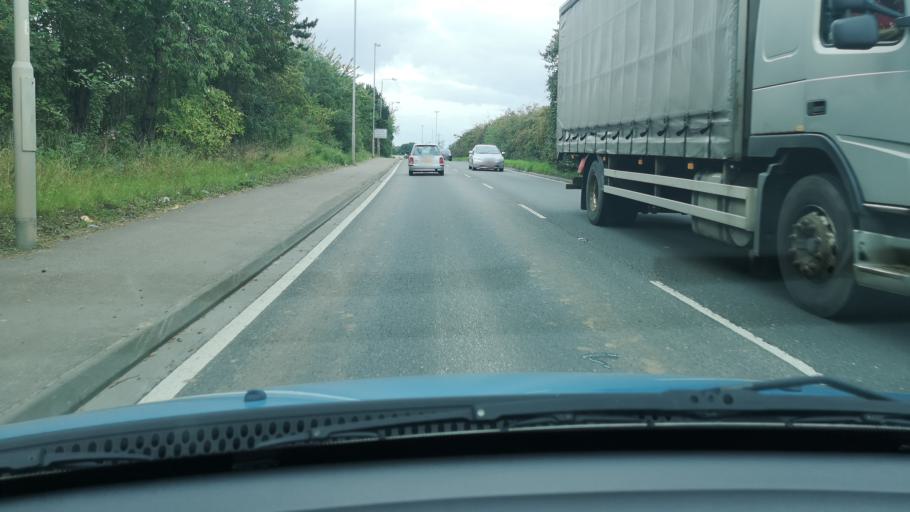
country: GB
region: England
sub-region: City and Borough of Wakefield
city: North Elmsall
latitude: 53.6060
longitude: -1.2738
